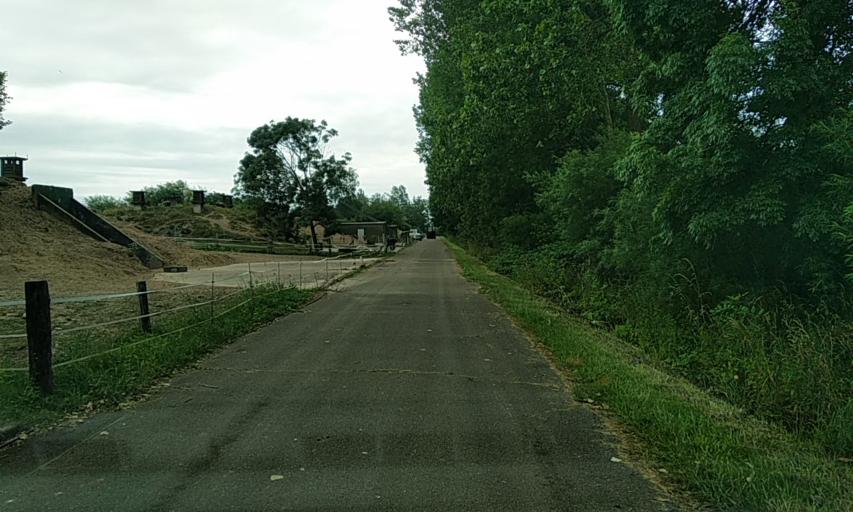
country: DE
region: Schleswig-Holstein
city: Brodersby
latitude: 54.6447
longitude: 10.0092
